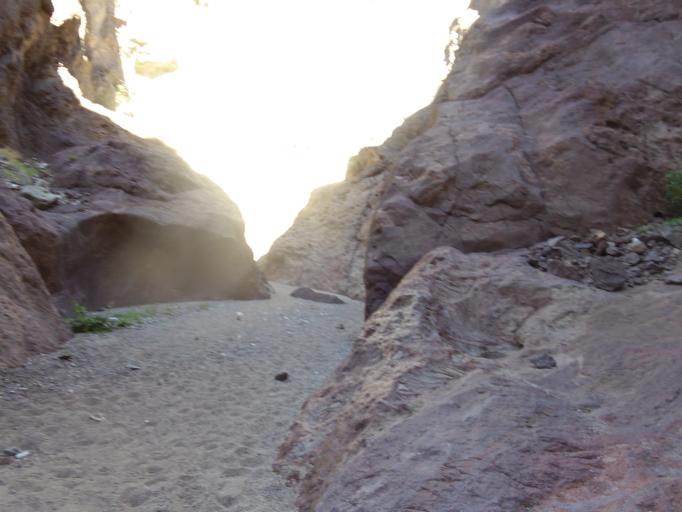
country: US
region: Nevada
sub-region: Clark County
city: Boulder City
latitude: 35.9733
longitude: -114.7166
